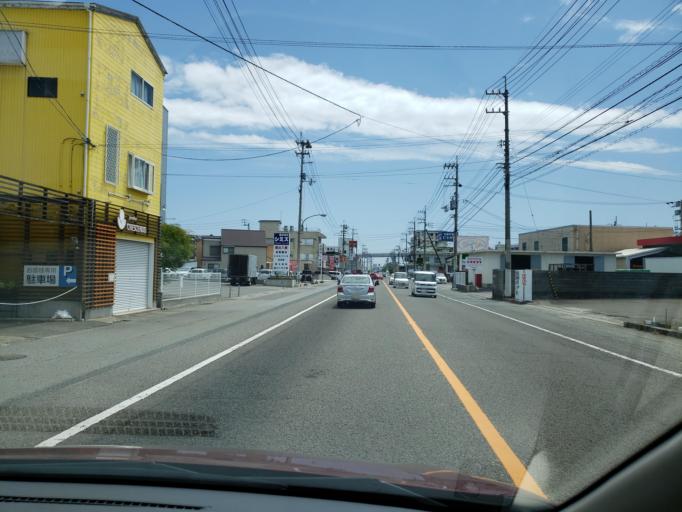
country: JP
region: Tokushima
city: Tokushima-shi
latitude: 34.0596
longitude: 134.5817
